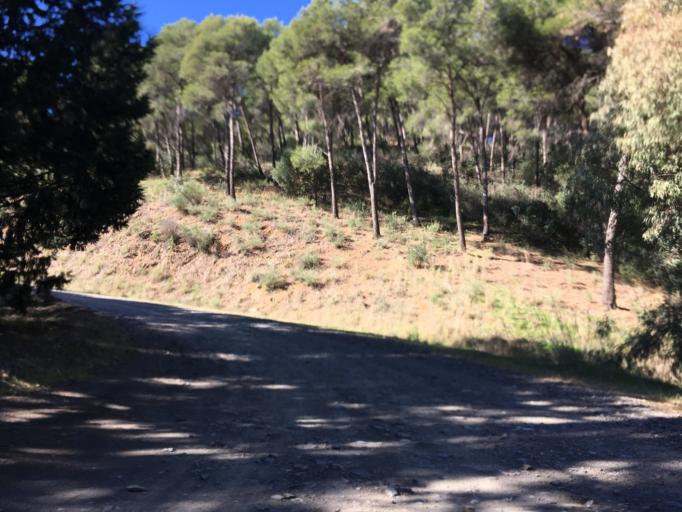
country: ES
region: Andalusia
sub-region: Provincia de Malaga
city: Malaga
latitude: 36.7824
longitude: -4.3865
